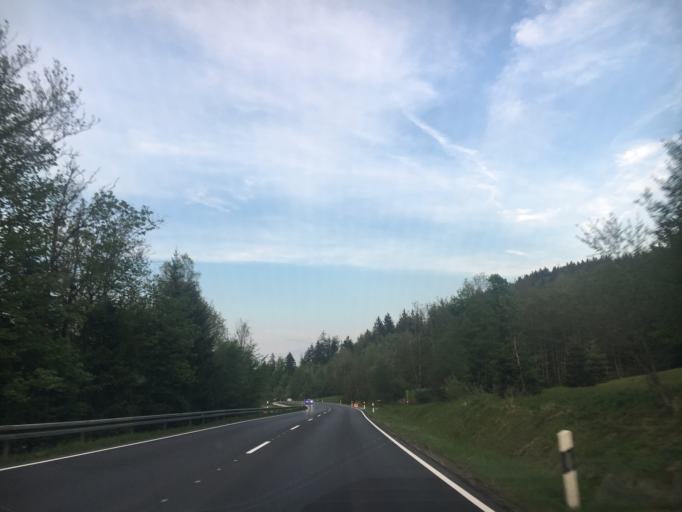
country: DE
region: Bavaria
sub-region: Upper Bavaria
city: Bad Heilbrunn
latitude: 47.7483
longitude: 11.4965
